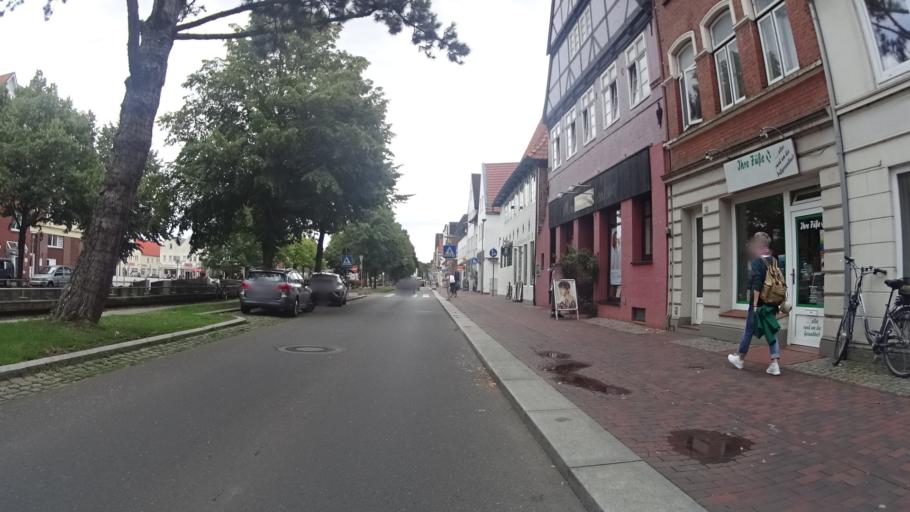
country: DE
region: Schleswig-Holstein
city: Gluckstadt
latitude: 53.7882
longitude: 9.4224
